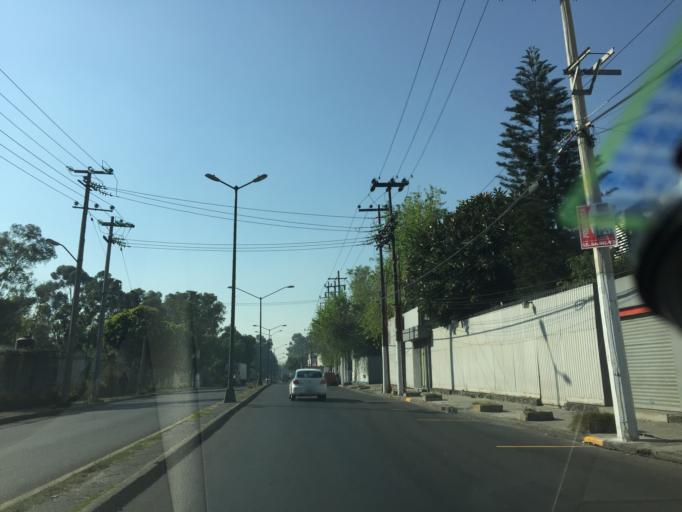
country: MX
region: Mexico
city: Vista Hermosa
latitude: 19.5015
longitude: -99.2126
